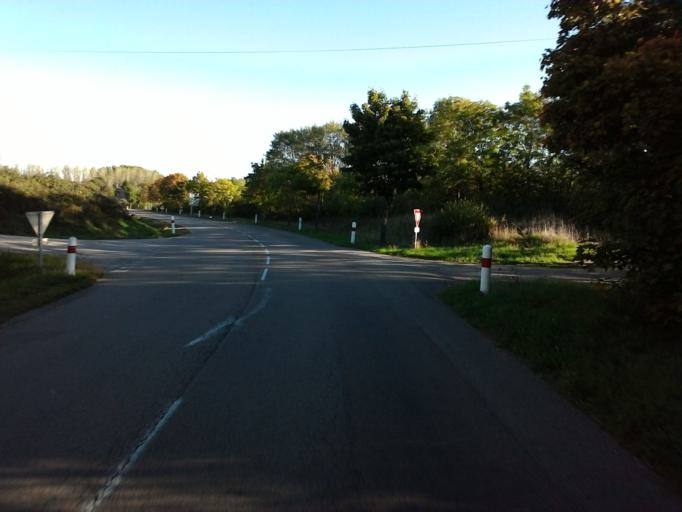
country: FR
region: Bourgogne
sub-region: Departement de la Cote-d'Or
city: Saulieu
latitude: 47.2747
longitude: 4.2386
